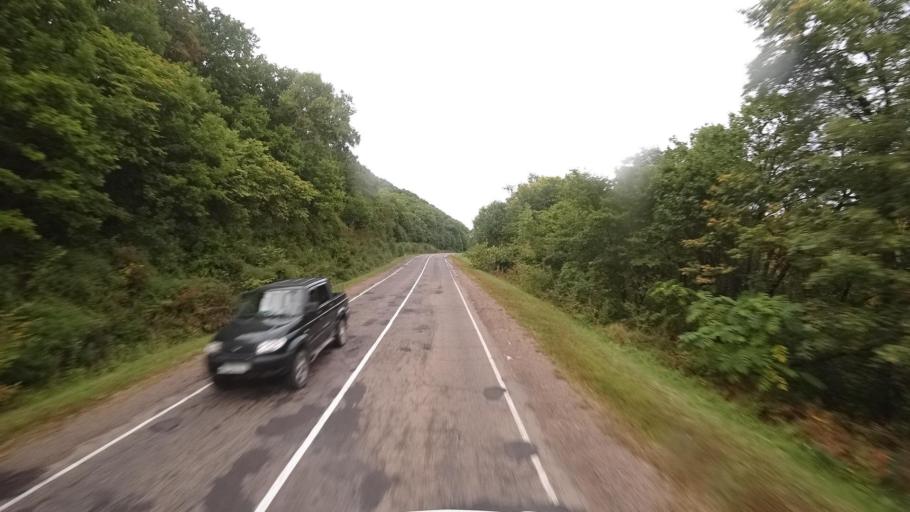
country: RU
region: Primorskiy
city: Yakovlevka
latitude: 44.3898
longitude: 133.4675
